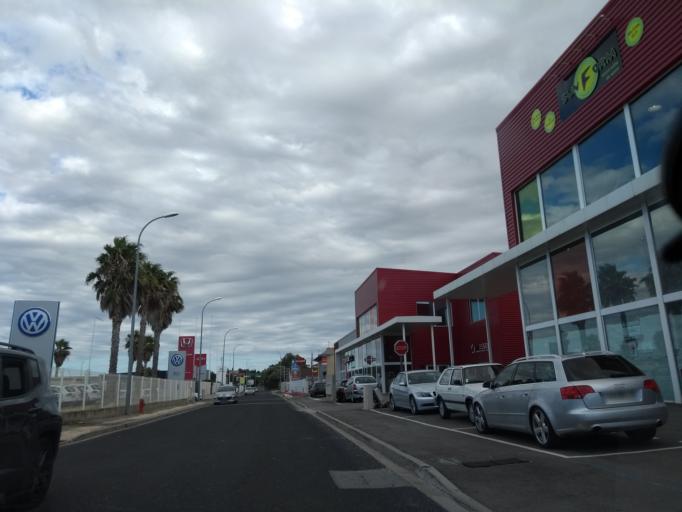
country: FR
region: Languedoc-Roussillon
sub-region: Departement des Pyrenees-Orientales
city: Perpignan
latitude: 42.6720
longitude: 2.8937
